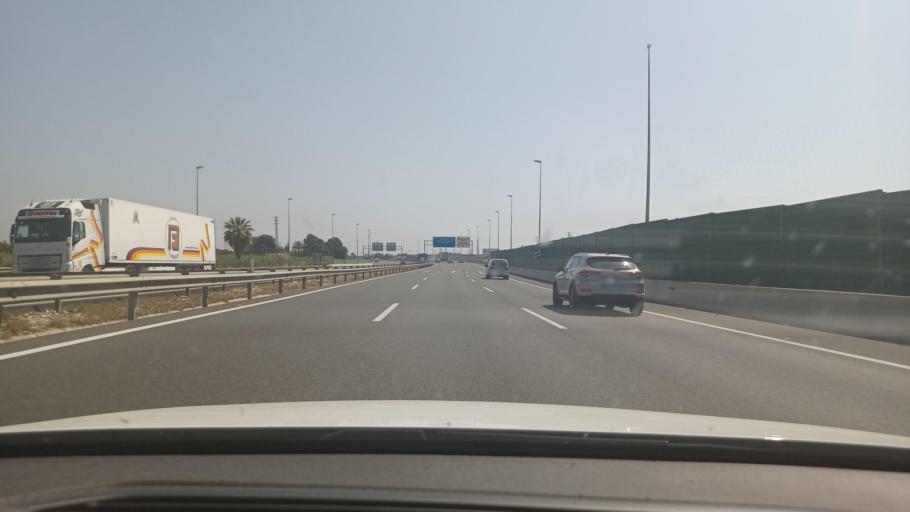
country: ES
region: Valencia
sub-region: Provincia de Alicante
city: Crevillente
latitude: 38.2262
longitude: -0.7969
